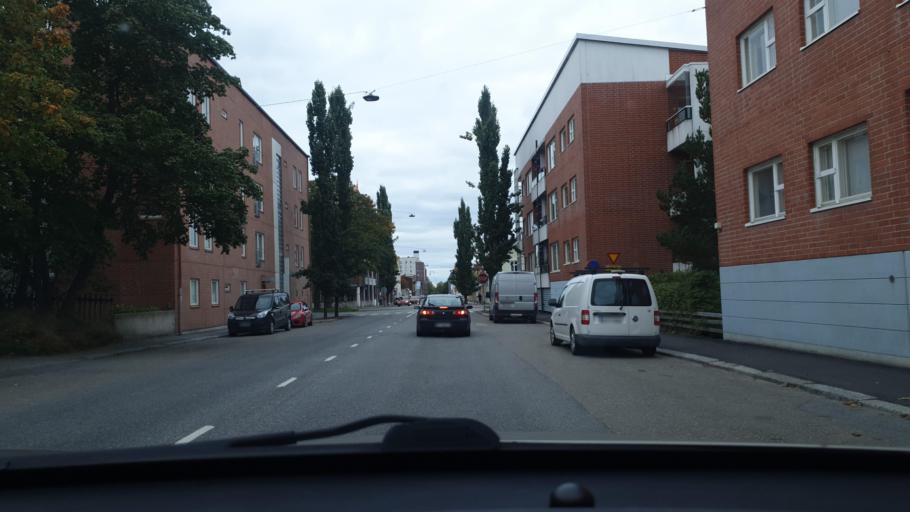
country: FI
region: Ostrobothnia
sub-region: Vaasa
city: Vaasa
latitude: 63.0910
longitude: 21.6266
